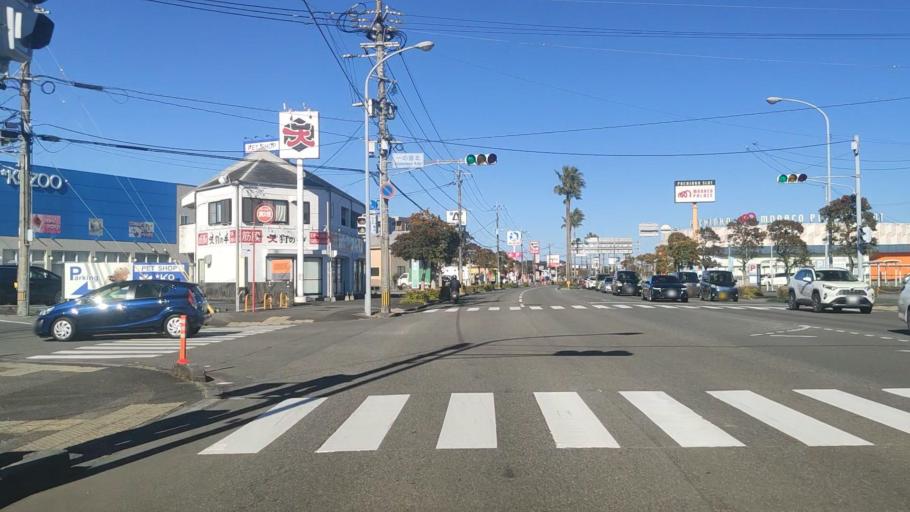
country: JP
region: Miyazaki
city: Miyazaki-shi
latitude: 31.9099
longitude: 131.4471
